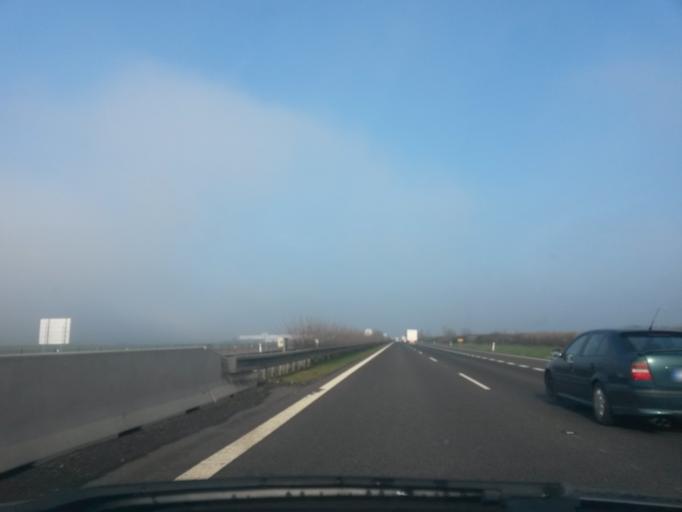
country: CZ
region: Ustecky
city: Postoloprty
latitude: 50.3705
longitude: 13.6236
